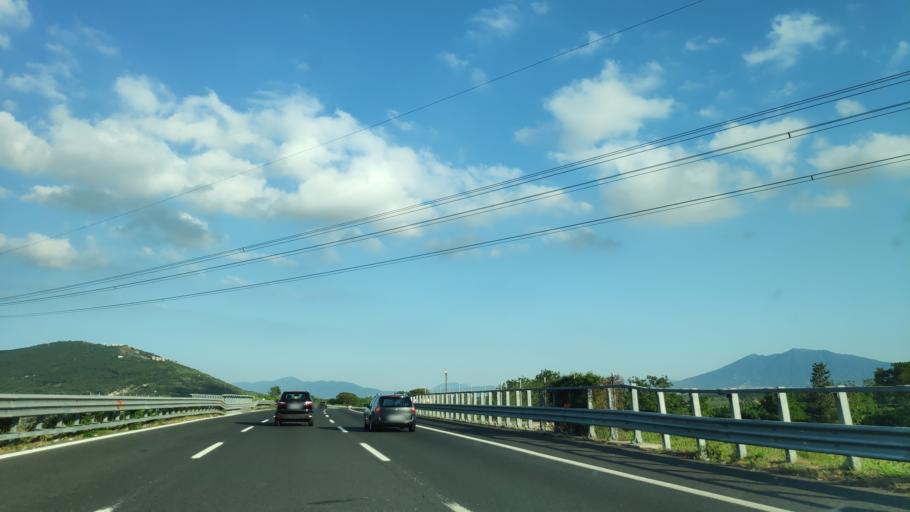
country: IT
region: Campania
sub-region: Provincia di Caserta
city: Montedecoro
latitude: 41.0075
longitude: 14.4013
